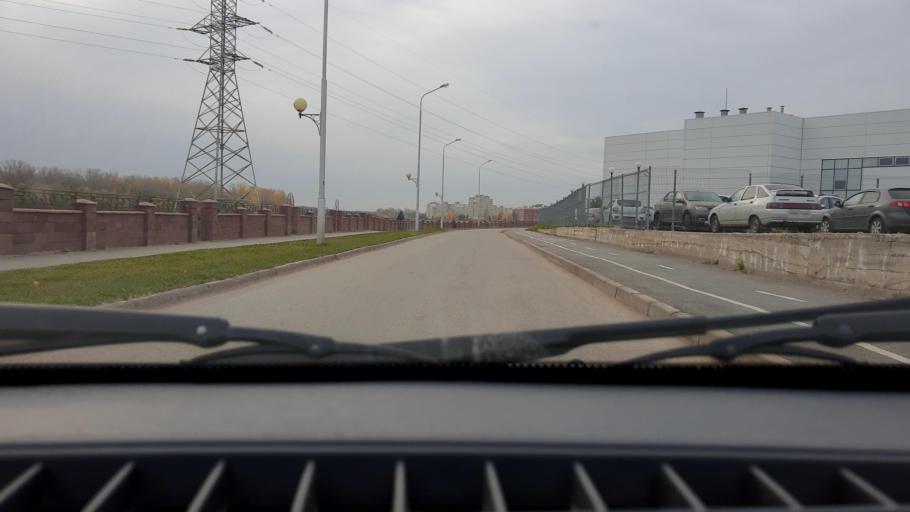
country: RU
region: Bashkortostan
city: Ufa
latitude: 54.7848
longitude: 56.0765
